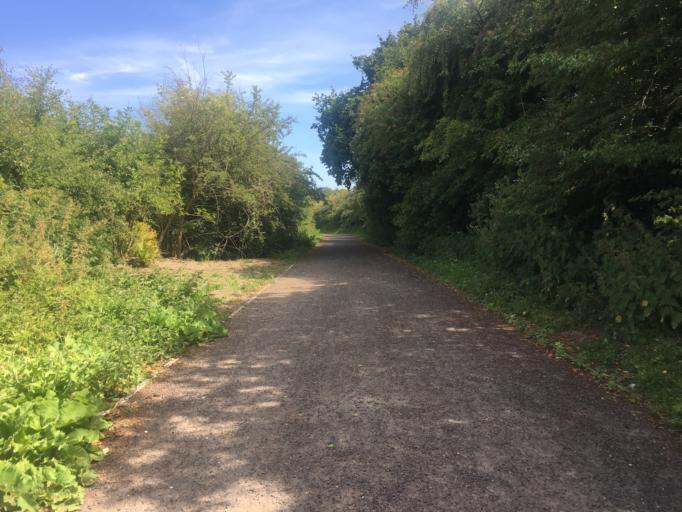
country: GB
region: England
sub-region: Sunderland
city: Washington
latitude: 54.8764
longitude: -1.5421
